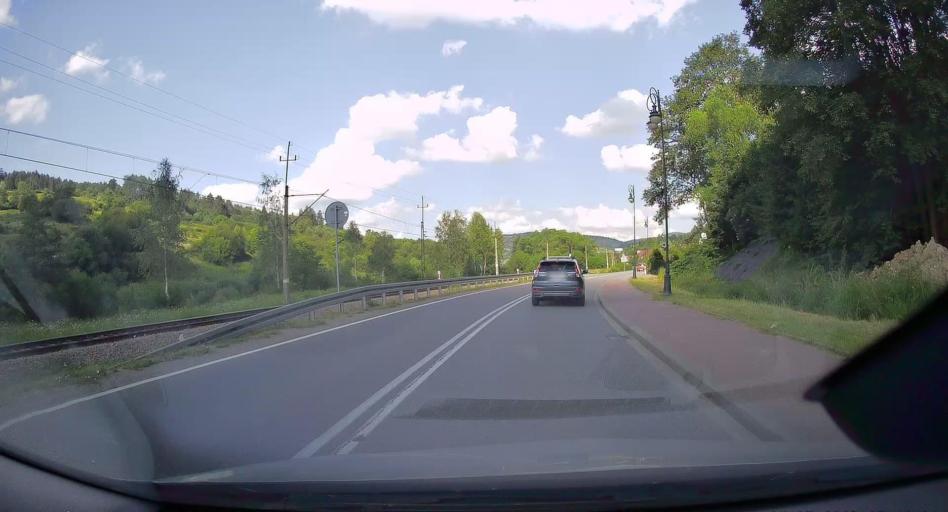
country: PL
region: Lesser Poland Voivodeship
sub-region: Powiat nowosadecki
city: Muszyna
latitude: 49.3640
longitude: 20.9279
